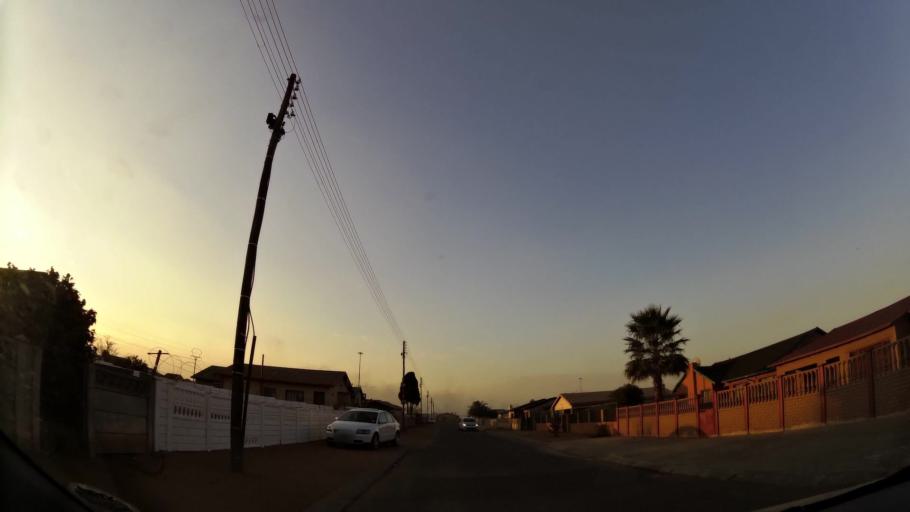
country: ZA
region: Gauteng
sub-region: West Rand District Municipality
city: Randfontein
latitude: -26.2036
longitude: 27.7082
